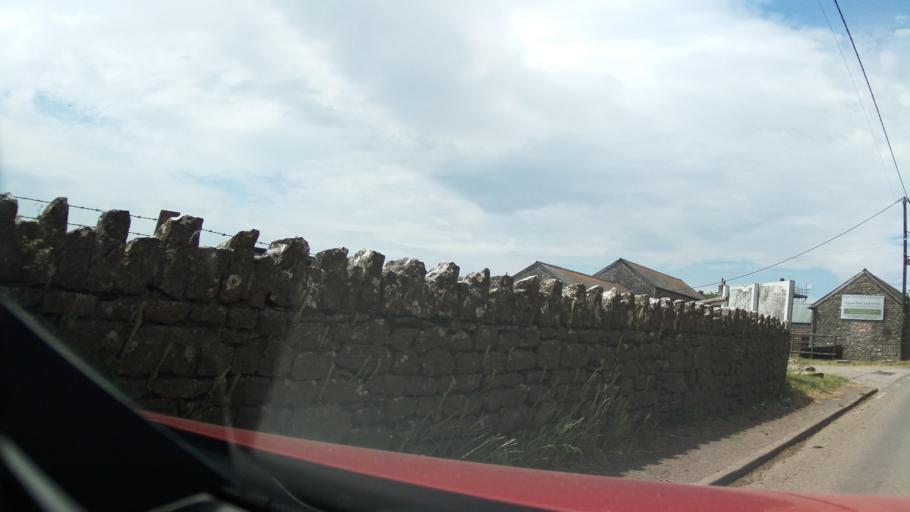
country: GB
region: Wales
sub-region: Vale of Glamorgan
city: Wick
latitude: 51.4537
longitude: -3.5859
